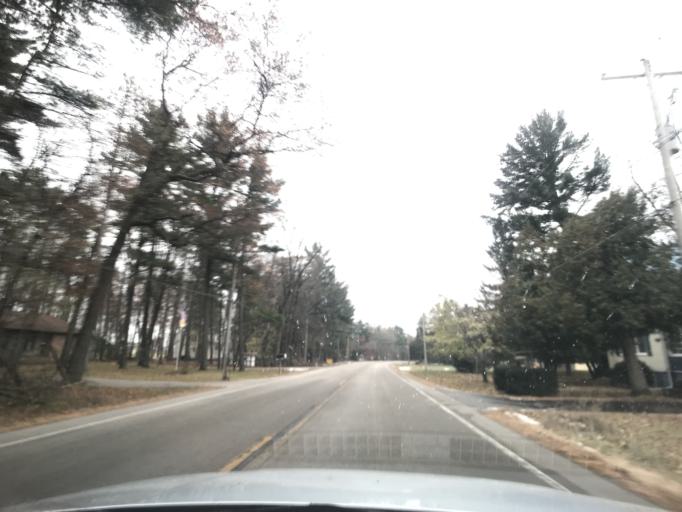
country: US
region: Wisconsin
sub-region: Marinette County
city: Marinette
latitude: 45.0642
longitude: -87.6193
